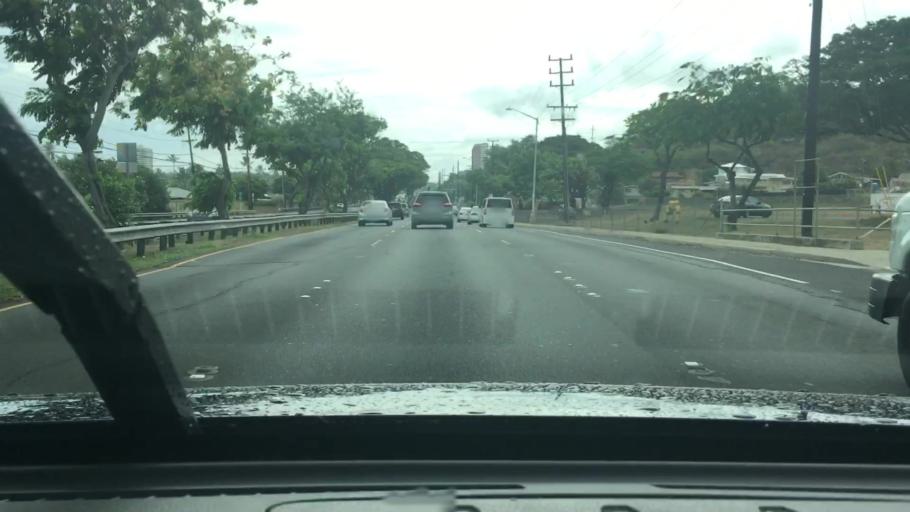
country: US
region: Hawaii
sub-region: Honolulu County
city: Waimanalo
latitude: 21.2773
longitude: -157.7735
